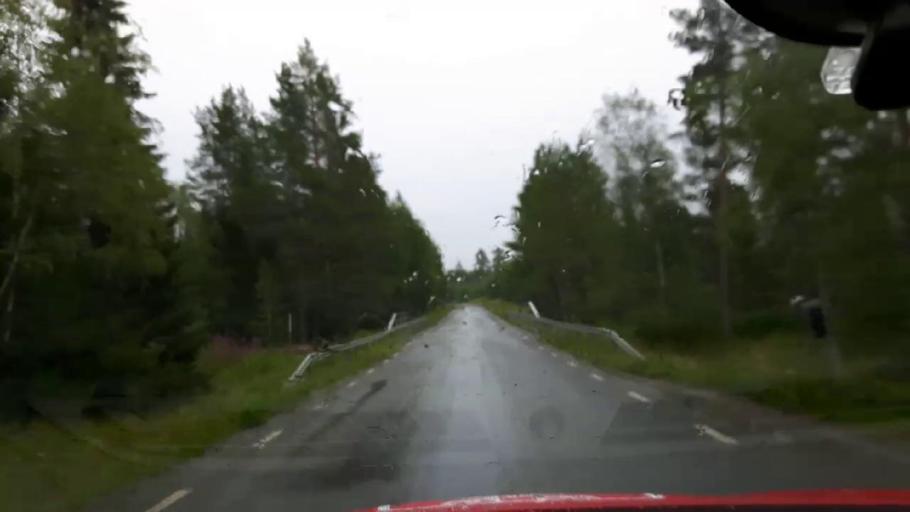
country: SE
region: Jaemtland
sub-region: OEstersunds Kommun
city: Brunflo
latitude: 62.9808
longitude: 14.8246
